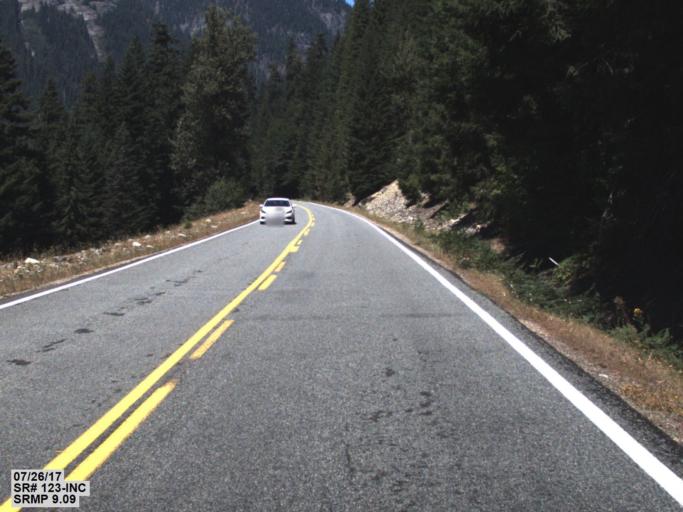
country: US
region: Washington
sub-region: King County
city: Enumclaw
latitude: 46.8052
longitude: -121.5547
